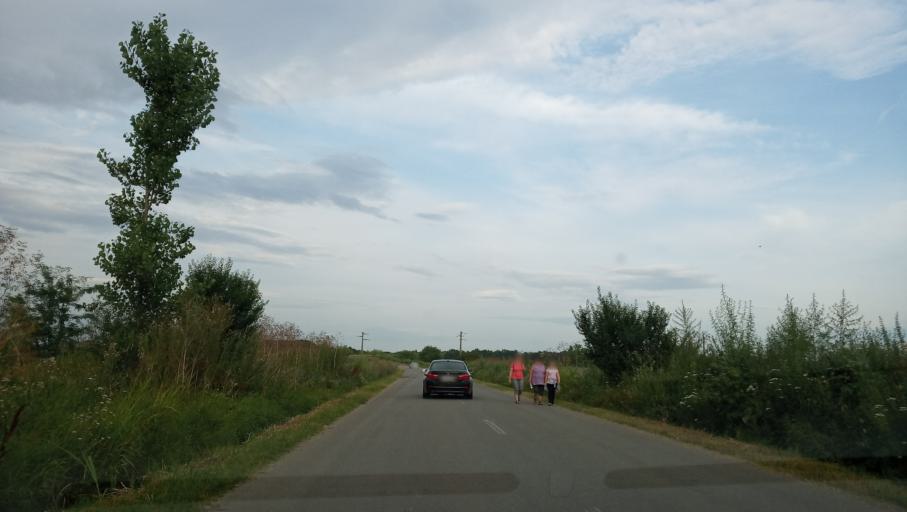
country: RO
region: Giurgiu
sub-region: Comuna Singureni
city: Singureni
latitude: 44.2289
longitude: 25.9285
